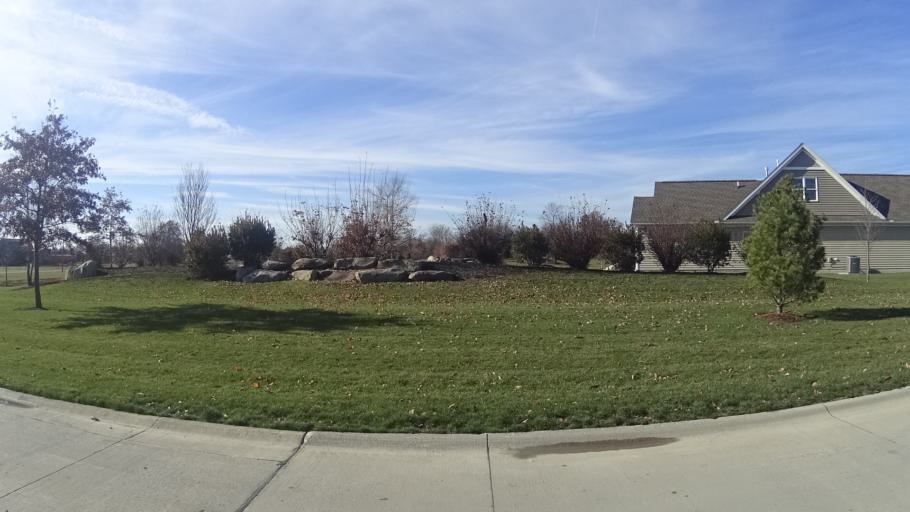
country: US
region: Ohio
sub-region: Lorain County
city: Eaton Estates
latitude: 41.3147
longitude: -81.9943
